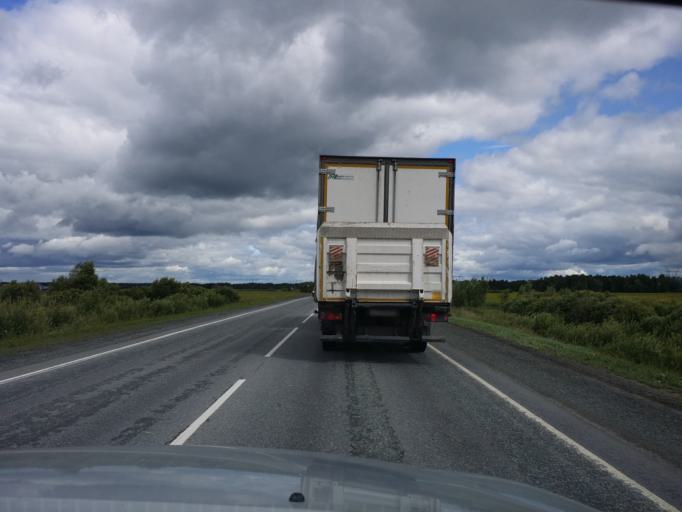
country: RU
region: Tjumen
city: Sumkino
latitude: 57.9214
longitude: 68.1511
